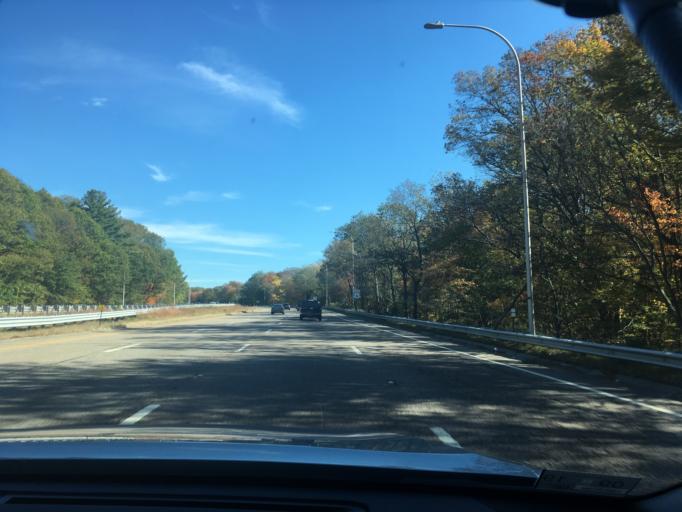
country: US
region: Rhode Island
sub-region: Providence County
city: Johnston
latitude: 41.8167
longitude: -71.4925
